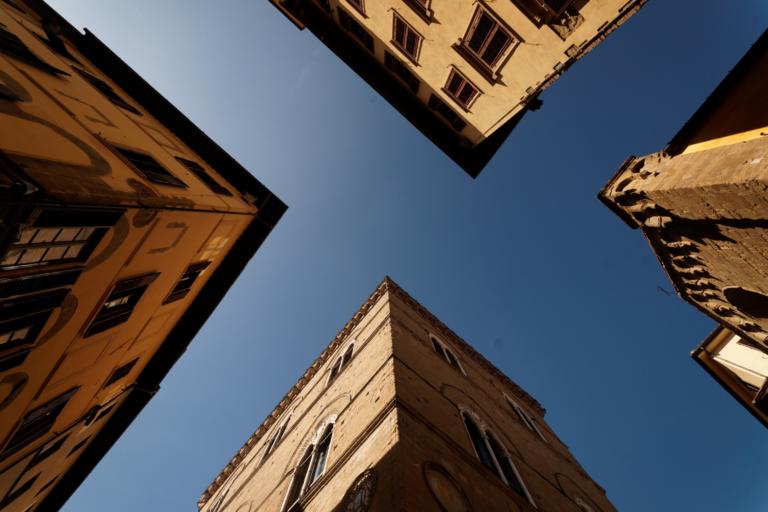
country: IT
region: Tuscany
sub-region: Province of Florence
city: Florence
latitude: 43.7705
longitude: 11.2553
